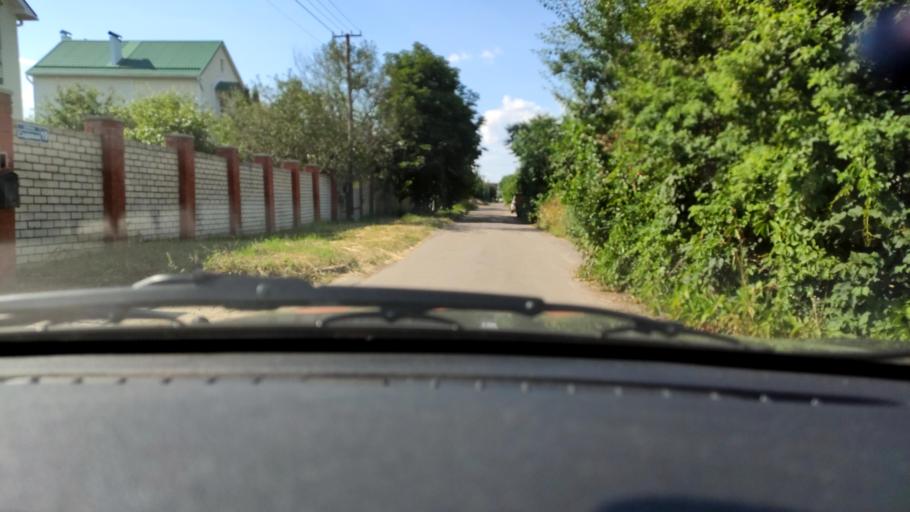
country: RU
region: Voronezj
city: Ramon'
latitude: 51.8318
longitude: 39.2673
